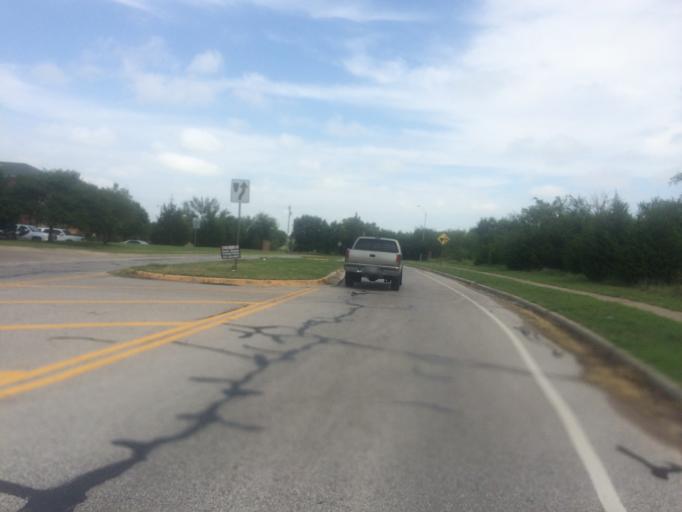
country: US
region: Oklahoma
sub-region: Cleveland County
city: Norman
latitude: 35.1906
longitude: -97.4253
